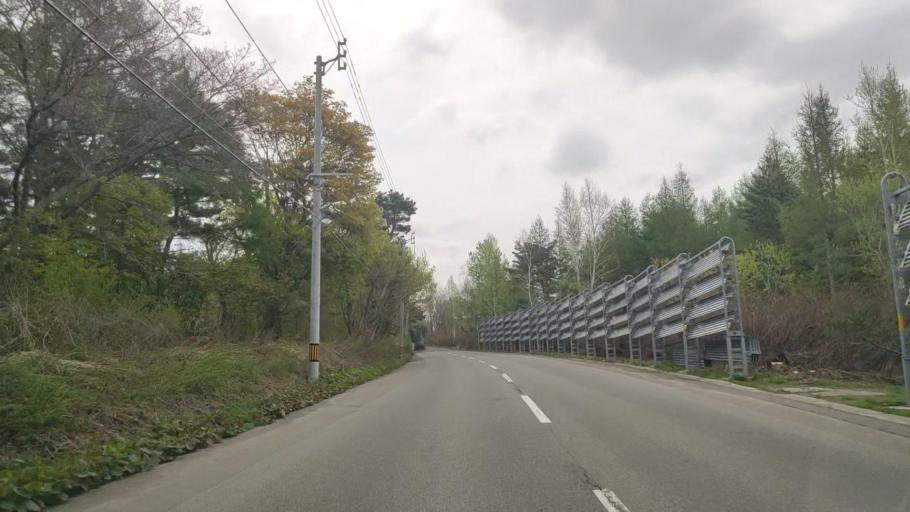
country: JP
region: Aomori
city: Aomori Shi
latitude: 40.7506
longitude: 140.8172
